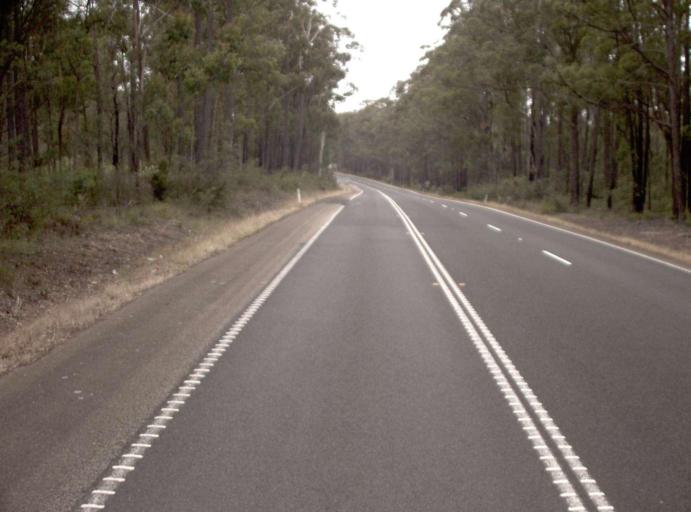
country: AU
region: Victoria
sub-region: East Gippsland
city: Lakes Entrance
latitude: -37.7289
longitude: 147.9208
